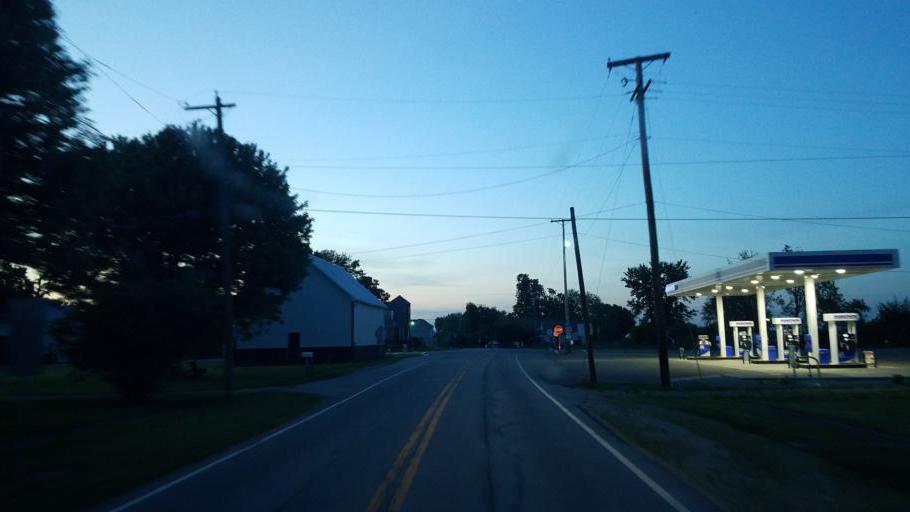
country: US
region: Ohio
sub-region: Highland County
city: Greenfield
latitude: 39.2191
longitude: -83.4215
